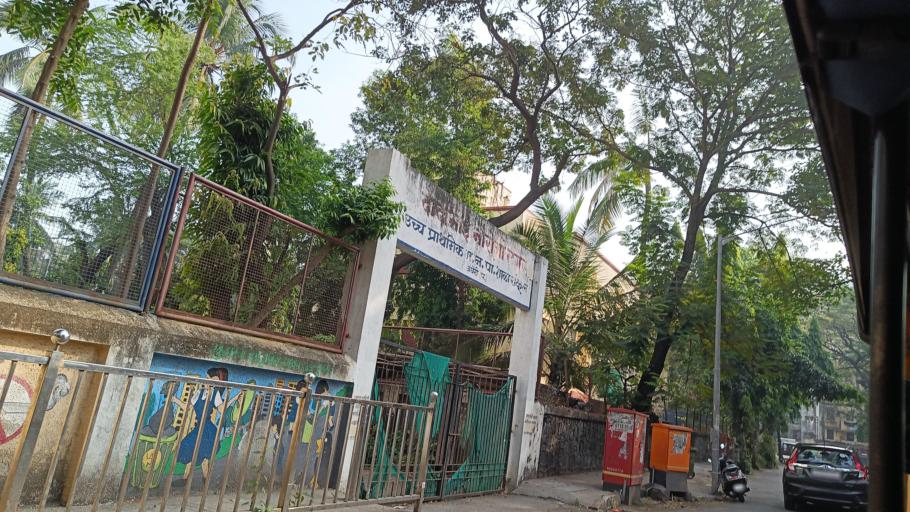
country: IN
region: Maharashtra
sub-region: Mumbai Suburban
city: Mumbai
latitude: 19.1235
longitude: 72.8294
